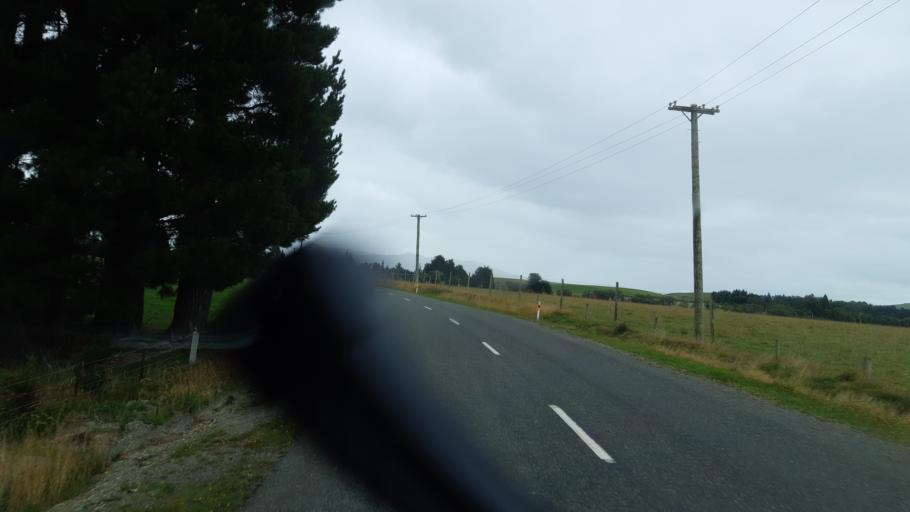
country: NZ
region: Southland
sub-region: Southland District
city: Winton
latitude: -45.7630
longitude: 168.5031
